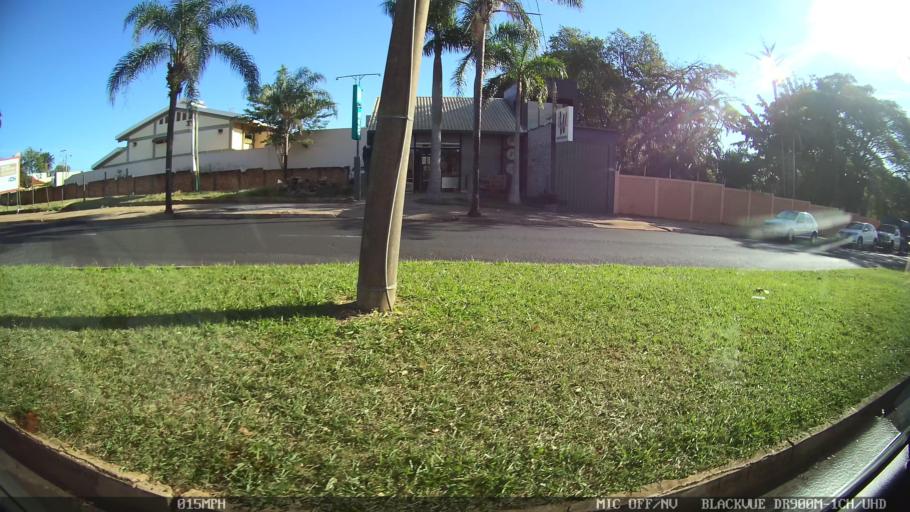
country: BR
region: Sao Paulo
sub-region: Araraquara
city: Araraquara
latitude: -21.7672
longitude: -48.1723
